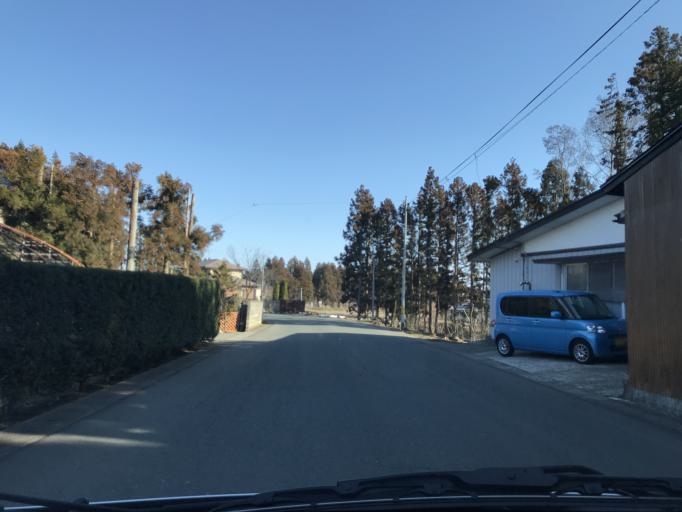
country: JP
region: Iwate
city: Kitakami
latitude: 39.2961
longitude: 141.0348
